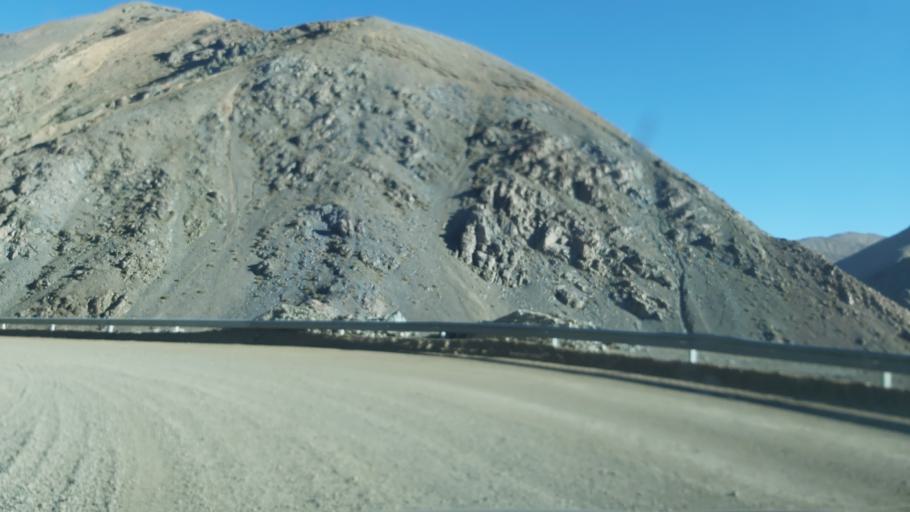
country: CL
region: Atacama
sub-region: Provincia de Chanaral
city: Diego de Almagro
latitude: -26.4793
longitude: -69.3204
